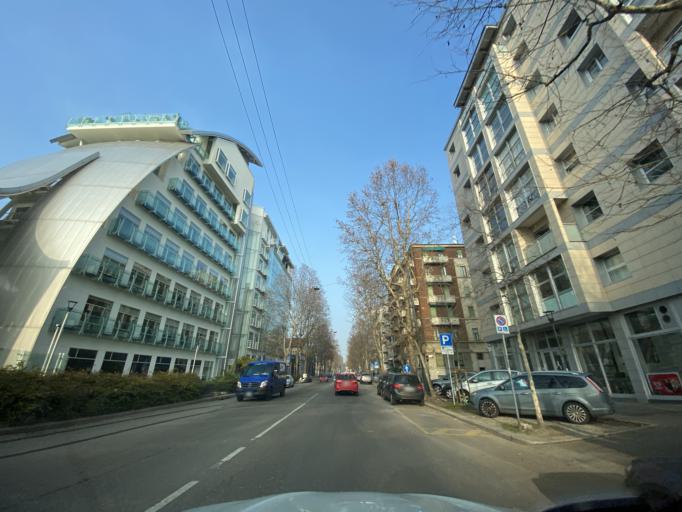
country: IT
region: Lombardy
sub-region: Citta metropolitana di Milano
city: Milano
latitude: 45.4934
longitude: 9.1825
